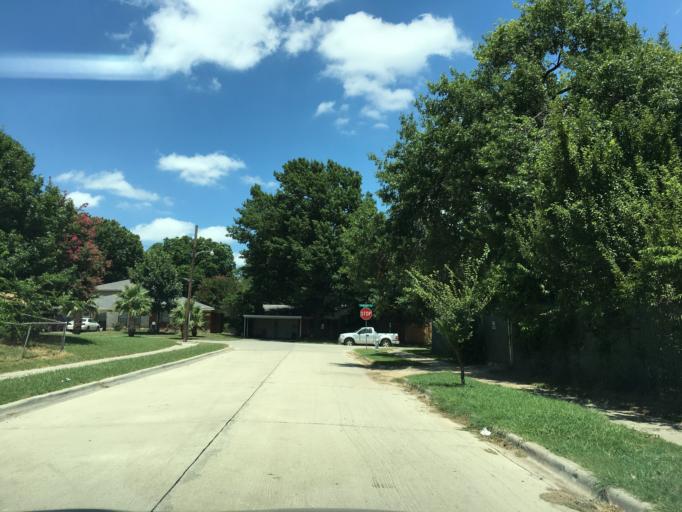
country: US
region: Texas
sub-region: Dallas County
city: Garland
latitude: 32.8338
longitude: -96.6490
